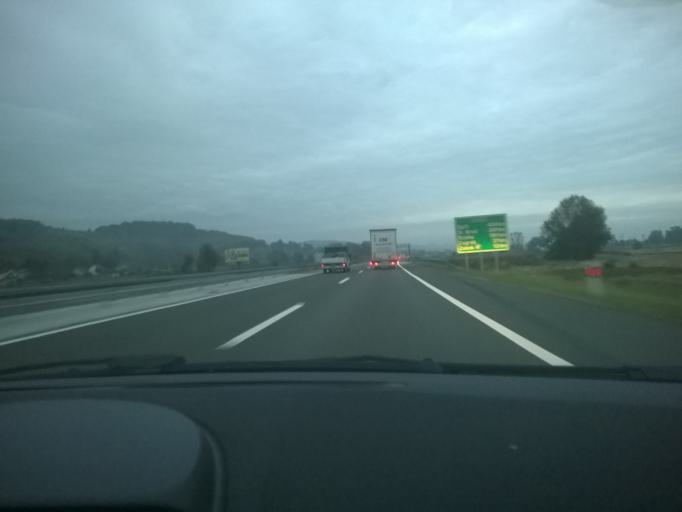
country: HR
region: Krapinsko-Zagorska
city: Zabok
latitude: 46.0862
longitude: 15.9112
